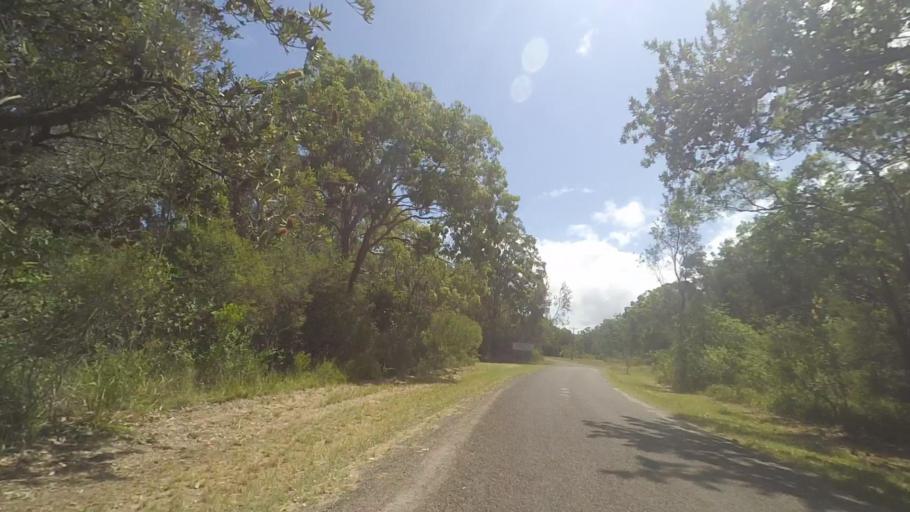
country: AU
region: New South Wales
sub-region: Great Lakes
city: Bulahdelah
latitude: -32.5089
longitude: 152.2973
